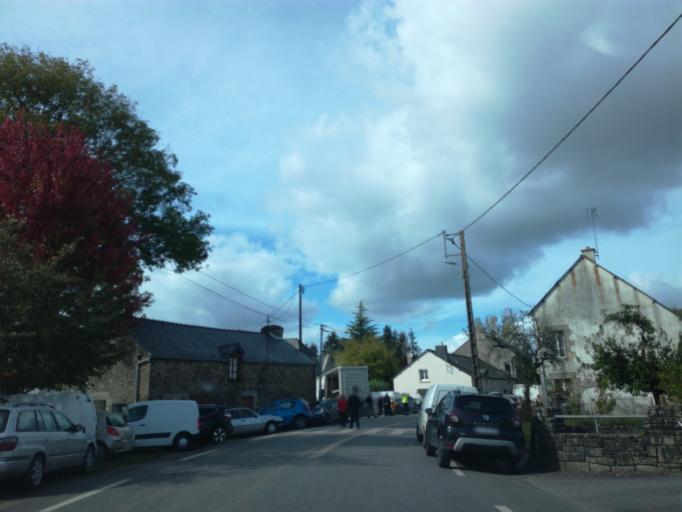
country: FR
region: Brittany
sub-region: Departement du Morbihan
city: Rohan
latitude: 48.0876
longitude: -2.7686
